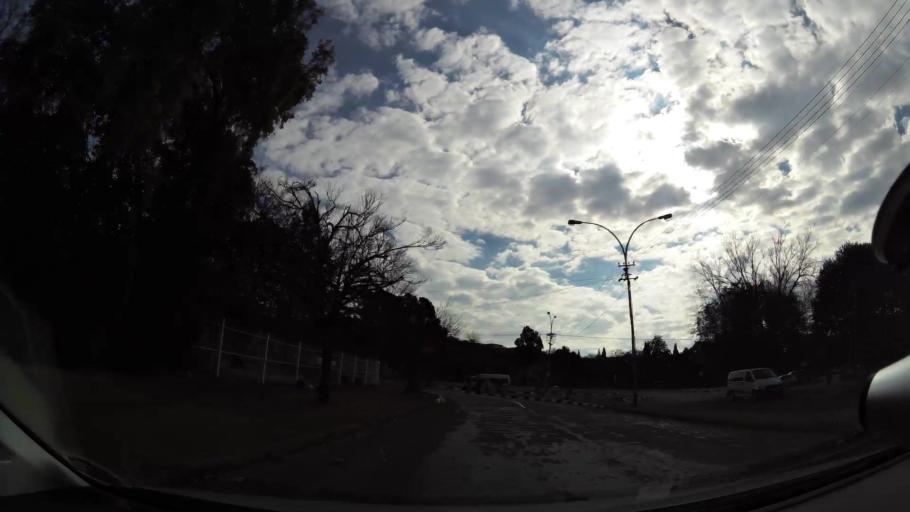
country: ZA
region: Orange Free State
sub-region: Mangaung Metropolitan Municipality
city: Bloemfontein
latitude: -29.0799
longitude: 26.2359
